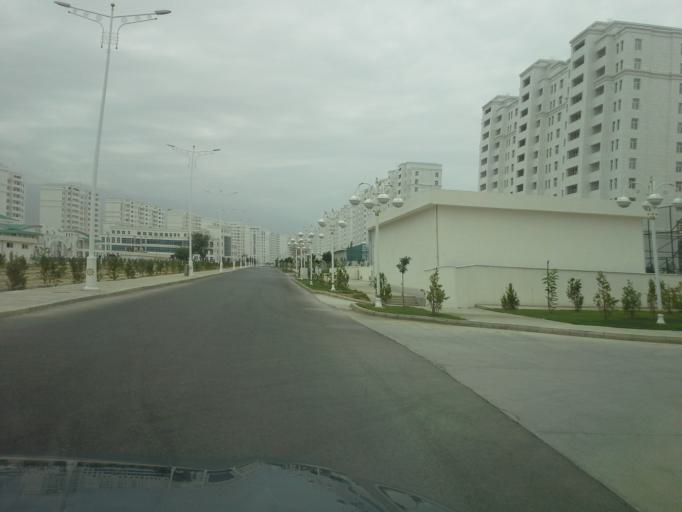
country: TM
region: Ahal
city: Ashgabat
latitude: 37.9187
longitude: 58.3648
